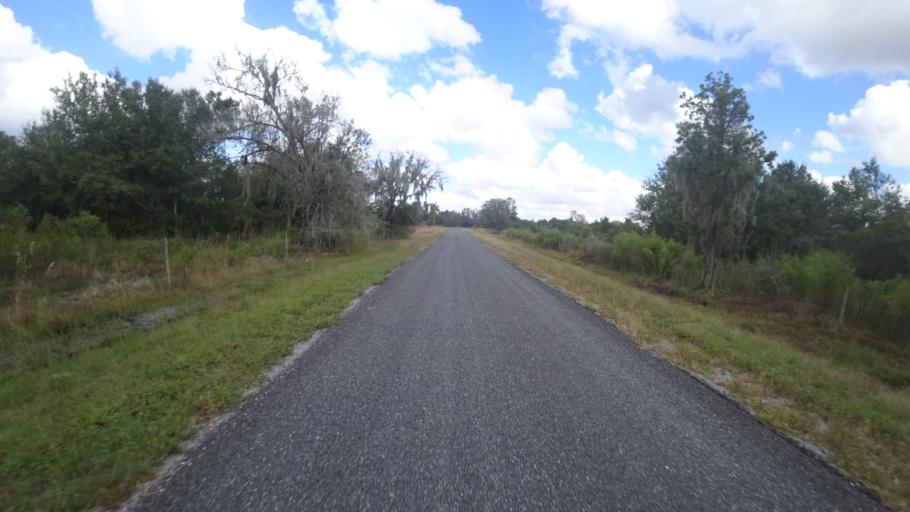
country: US
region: Florida
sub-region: Hillsborough County
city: Wimauma
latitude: 27.4868
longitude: -82.1707
